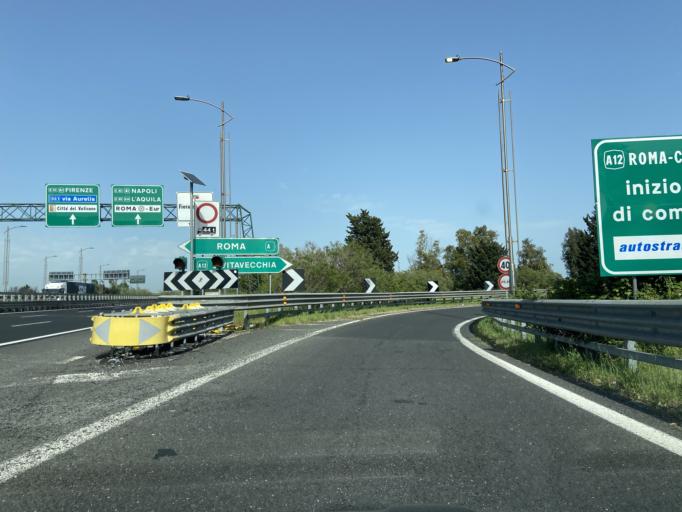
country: IT
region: Latium
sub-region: Citta metropolitana di Roma Capitale
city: Npp 23 (Parco Leonardo)
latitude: 41.8108
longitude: 12.3128
